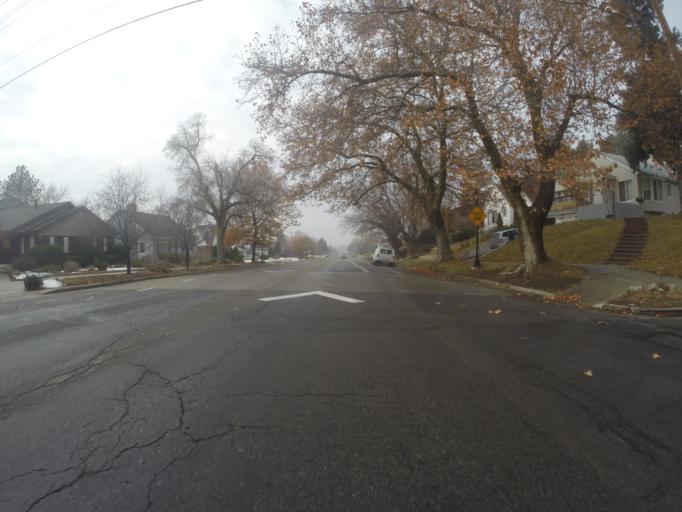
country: US
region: Utah
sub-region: Salt Lake County
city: Salt Lake City
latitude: 40.7819
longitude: -111.8745
